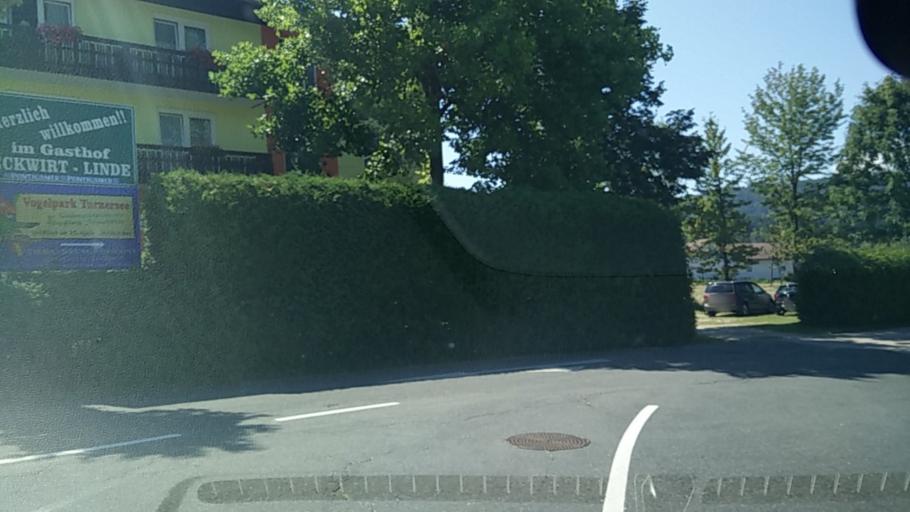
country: AT
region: Carinthia
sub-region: Politischer Bezirk Volkermarkt
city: Sittersdorf
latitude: 46.5795
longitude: 14.5636
